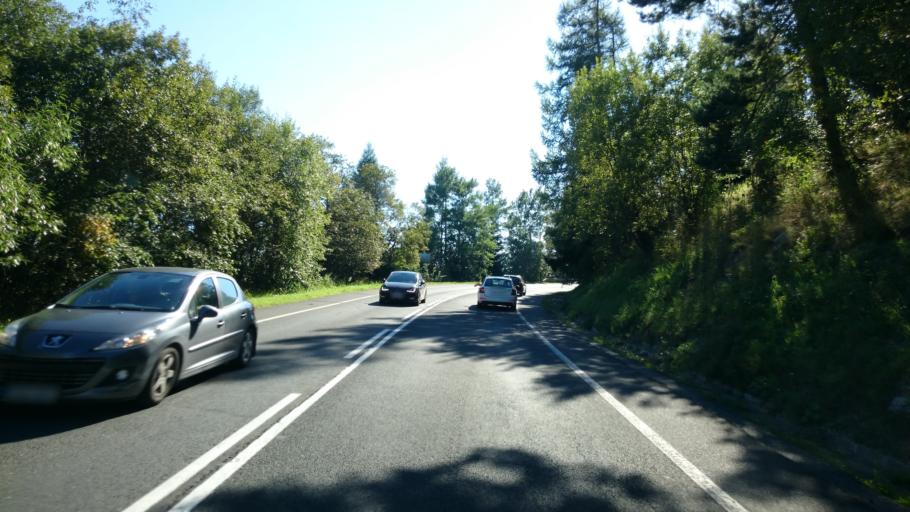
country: SK
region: Presovsky
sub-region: Okres Poprad
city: Vysoke Tatry
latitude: 49.1409
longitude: 20.2373
